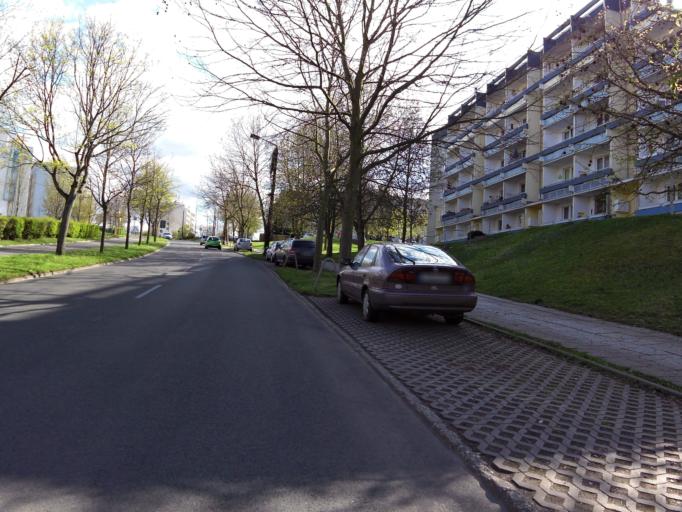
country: DE
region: Thuringia
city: Gotha
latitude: 50.9477
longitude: 10.6848
